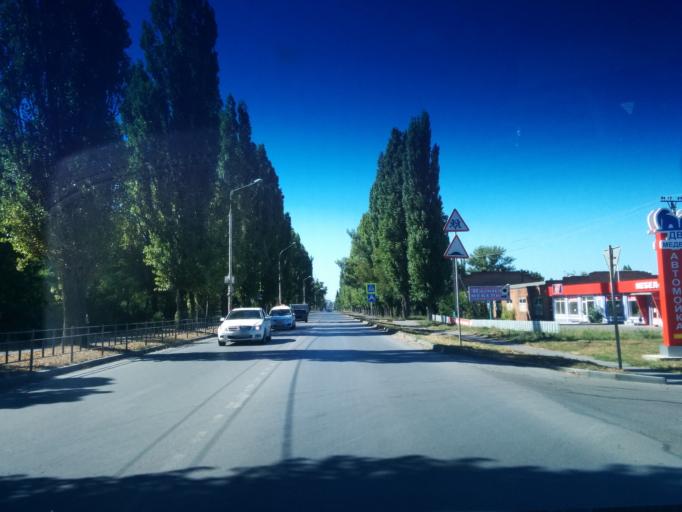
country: RU
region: Rostov
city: Shakhty
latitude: 47.6904
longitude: 40.2545
